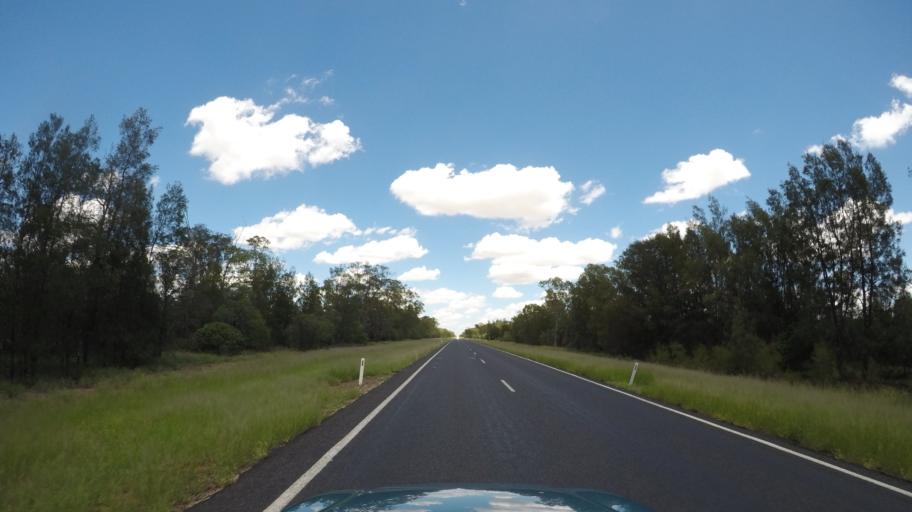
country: AU
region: Queensland
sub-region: Goondiwindi
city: Goondiwindi
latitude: -28.1659
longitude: 150.6046
